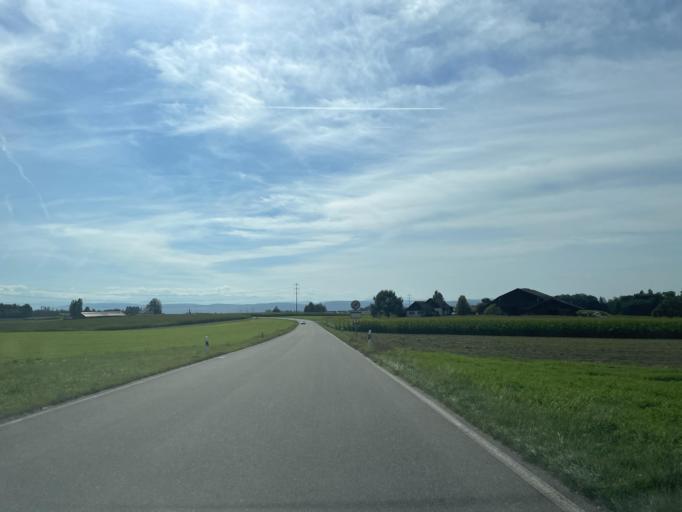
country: CH
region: Zurich
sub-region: Bezirk Winterthur
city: Brutten
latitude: 47.4695
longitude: 8.6689
